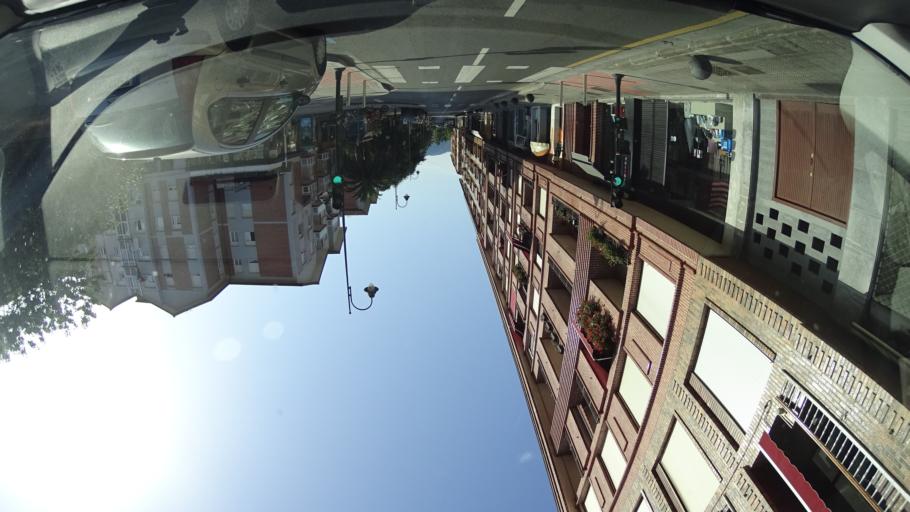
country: ES
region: Basque Country
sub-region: Bizkaia
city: Gernika-Lumo
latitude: 43.3089
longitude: -2.6799
